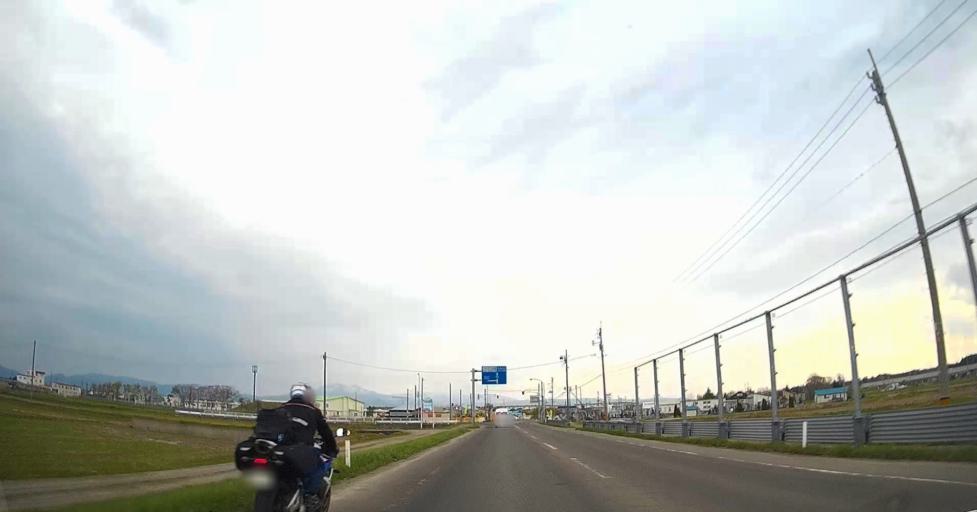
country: JP
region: Aomori
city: Aomori Shi
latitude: 40.8633
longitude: 140.6805
